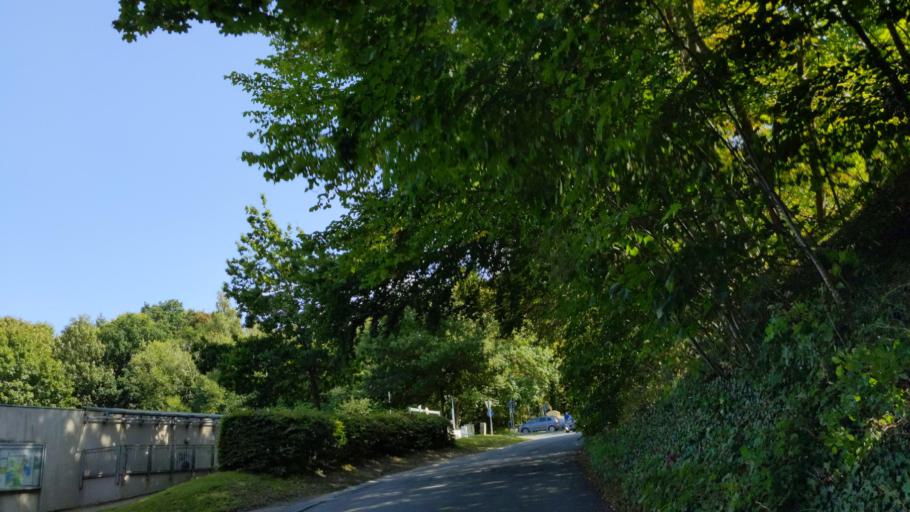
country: DE
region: Schleswig-Holstein
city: Malente
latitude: 54.1657
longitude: 10.5510
